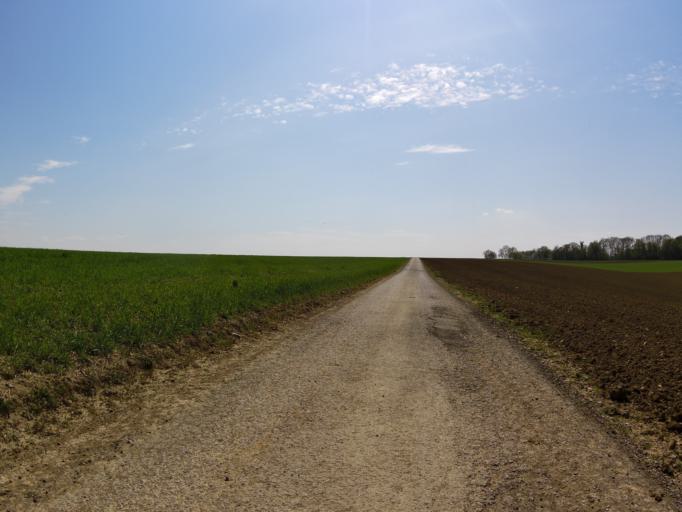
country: DE
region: Bavaria
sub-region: Regierungsbezirk Unterfranken
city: Giebelstadt
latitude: 49.6953
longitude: 9.9532
